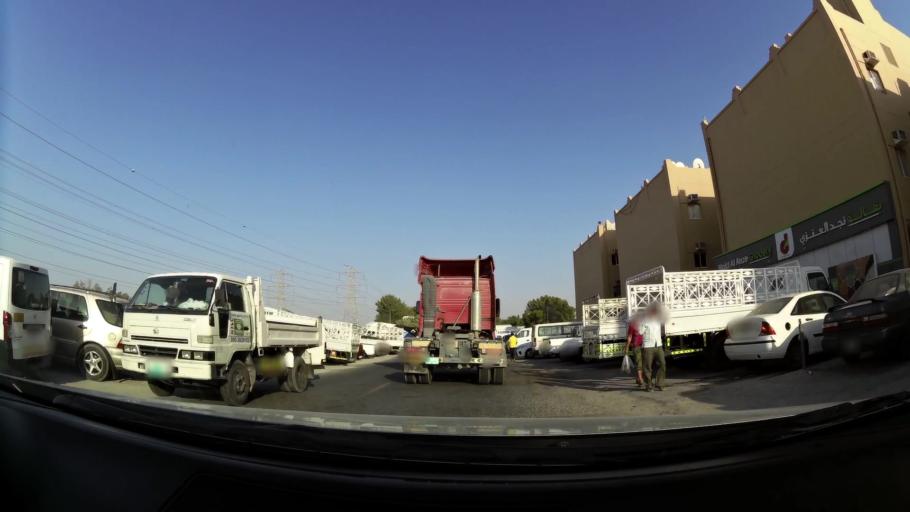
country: AE
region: Dubai
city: Dubai
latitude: 25.1343
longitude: 55.2405
